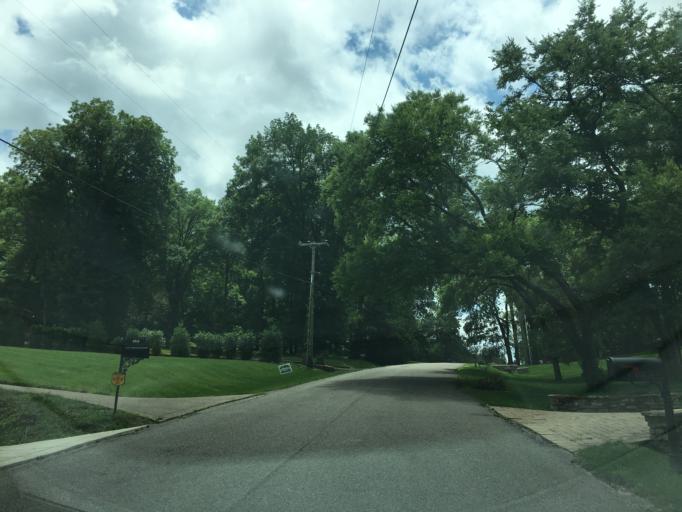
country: US
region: Tennessee
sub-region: Davidson County
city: Belle Meade
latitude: 36.0879
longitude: -86.8462
